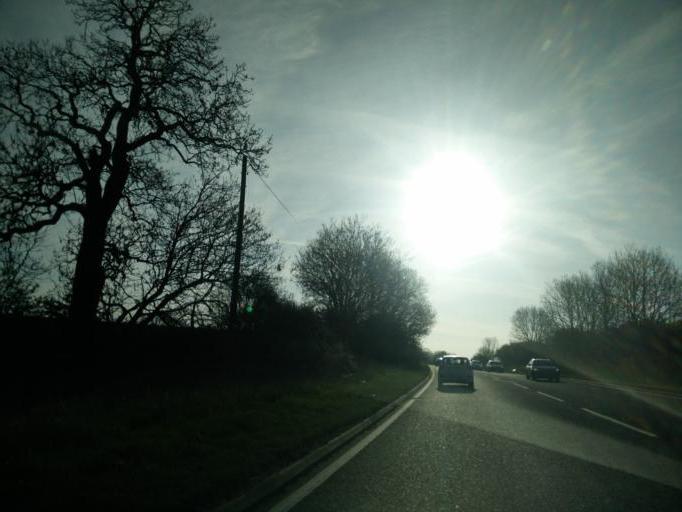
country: GB
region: England
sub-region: County Durham
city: Bishop Middleham
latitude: 54.6489
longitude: -1.5000
